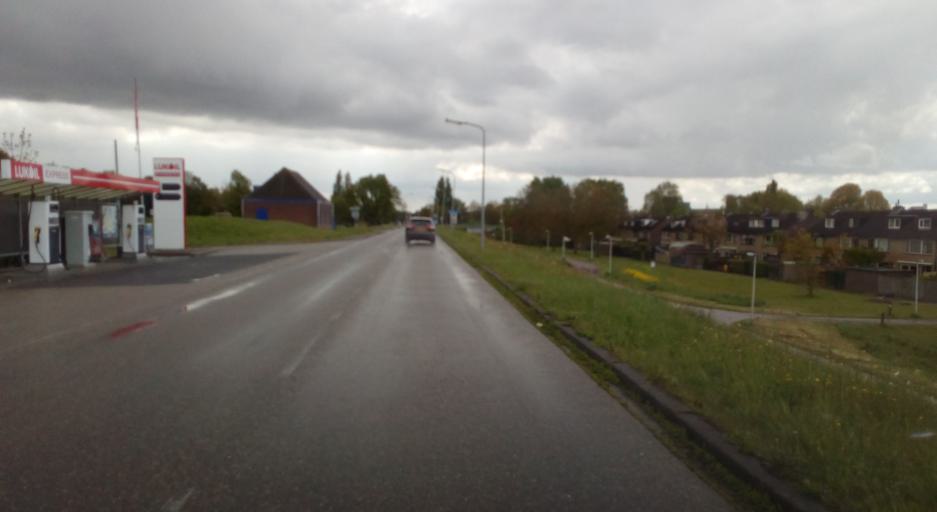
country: NL
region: South Holland
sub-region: Gemeente Dordrecht
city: Dordrecht
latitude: 51.8284
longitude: 4.6618
